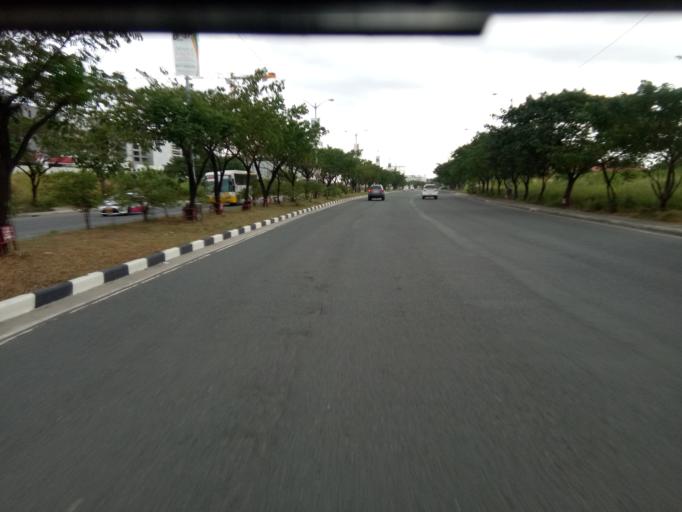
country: PH
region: Metro Manila
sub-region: Makati City
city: Makati City
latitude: 14.5136
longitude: 120.9902
